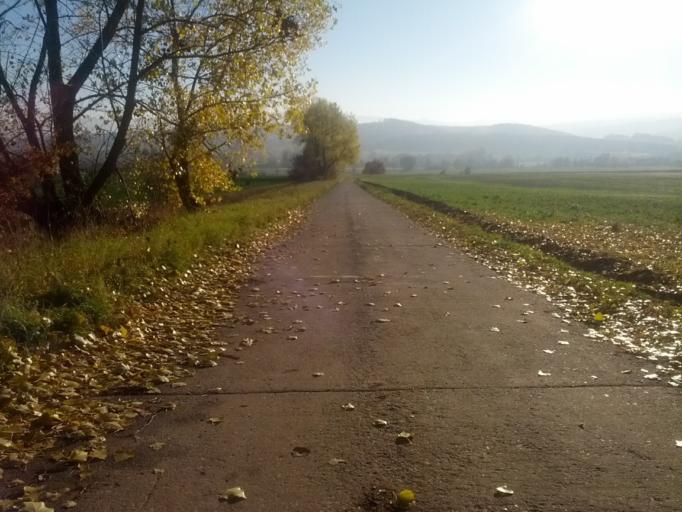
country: DE
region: Thuringia
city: Mechterstadt
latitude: 50.9525
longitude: 10.5138
